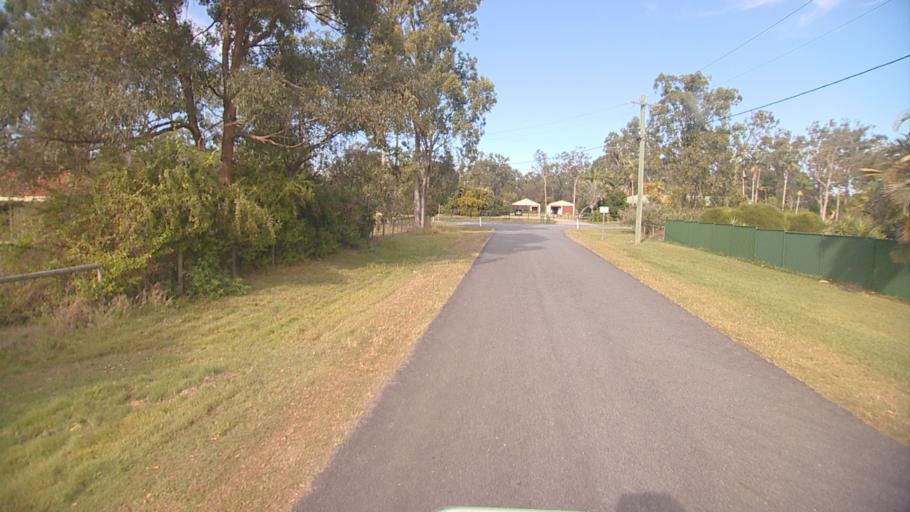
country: AU
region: Queensland
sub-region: Logan
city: Park Ridge South
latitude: -27.7417
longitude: 153.0433
